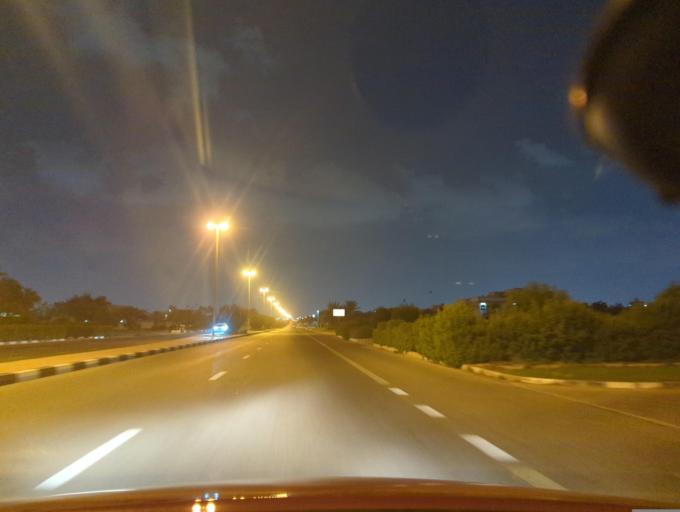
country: AE
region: Ash Shariqah
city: Sharjah
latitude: 25.3582
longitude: 55.4696
